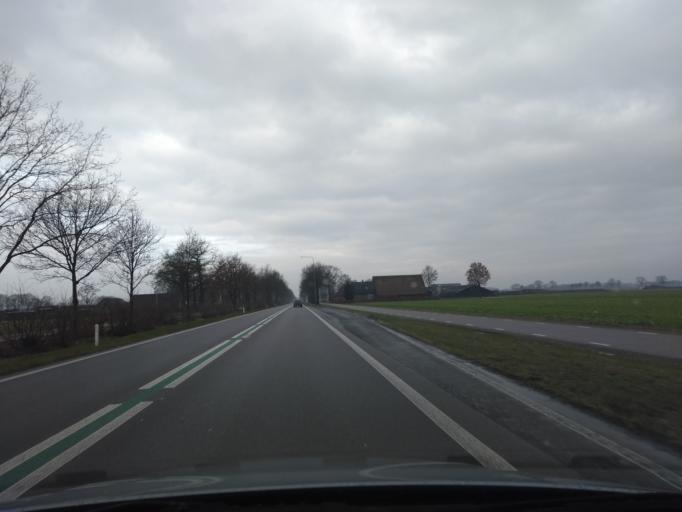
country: NL
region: Overijssel
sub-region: Gemeente Dalfsen
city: Dalfsen
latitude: 52.5976
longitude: 6.3643
